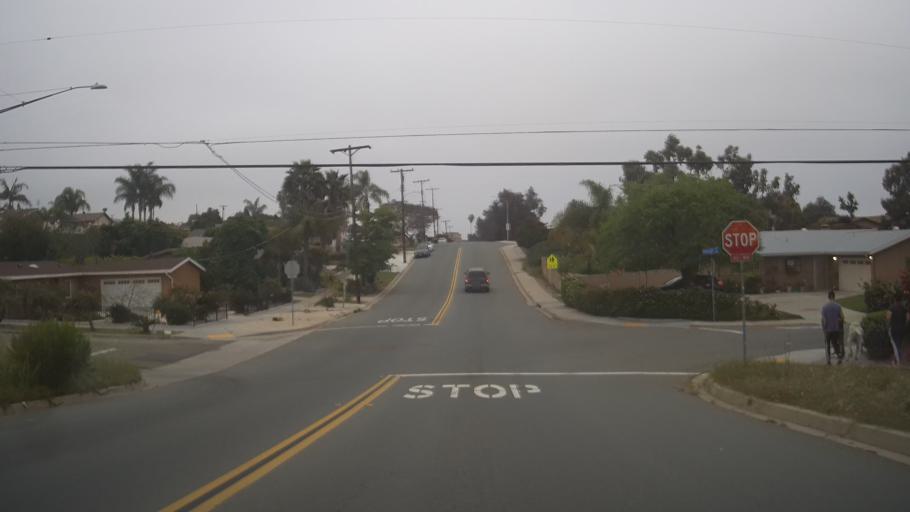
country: US
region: California
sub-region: San Diego County
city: Bonita
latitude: 32.6233
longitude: -117.0480
